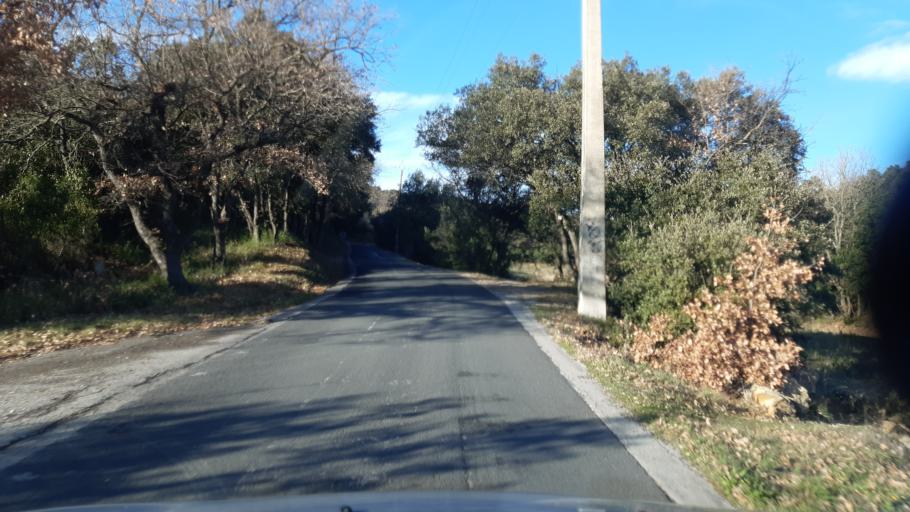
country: FR
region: Languedoc-Roussillon
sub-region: Departement de l'Herault
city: Murviel-les-Montpellier
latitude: 43.6158
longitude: 3.7413
